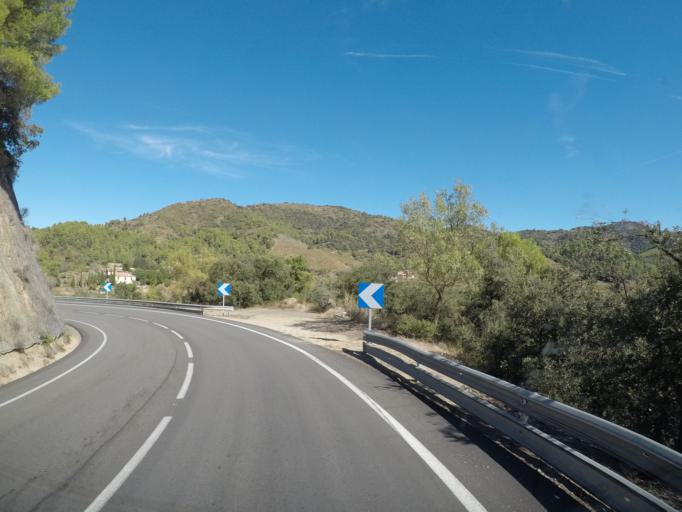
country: ES
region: Catalonia
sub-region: Provincia de Tarragona
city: Falset
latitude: 41.1664
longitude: 0.8201
